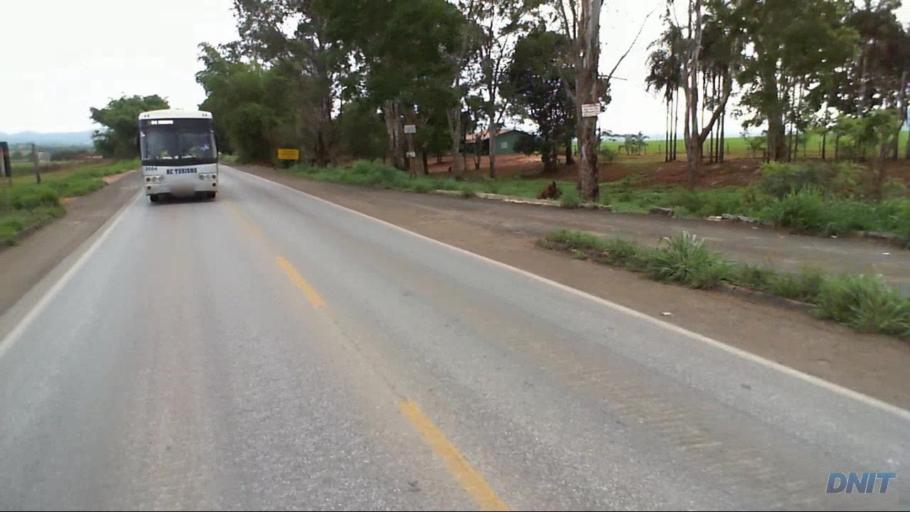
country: BR
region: Goias
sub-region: Uruacu
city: Uruacu
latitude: -14.6285
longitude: -49.1737
